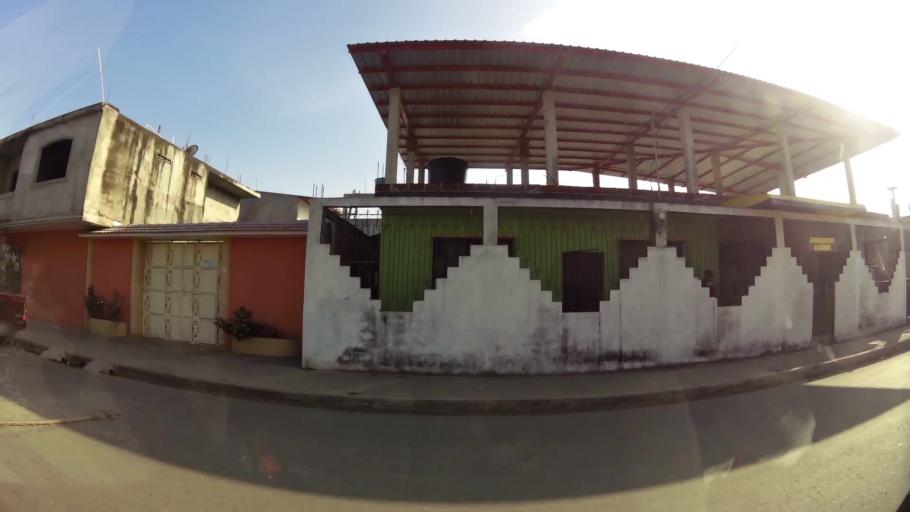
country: EC
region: Guayas
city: Eloy Alfaro
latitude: -2.1838
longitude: -79.8437
